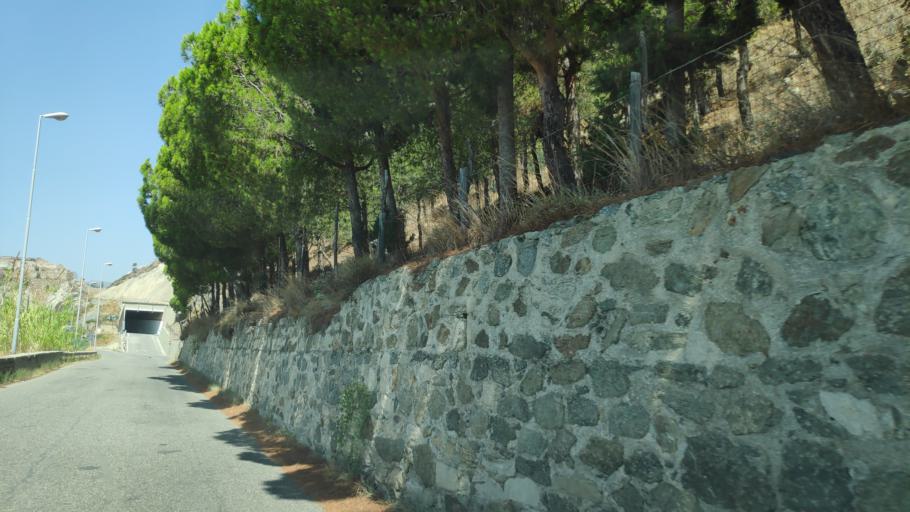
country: IT
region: Calabria
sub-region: Provincia di Reggio Calabria
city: Bova Marina
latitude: 37.9279
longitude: 15.9345
